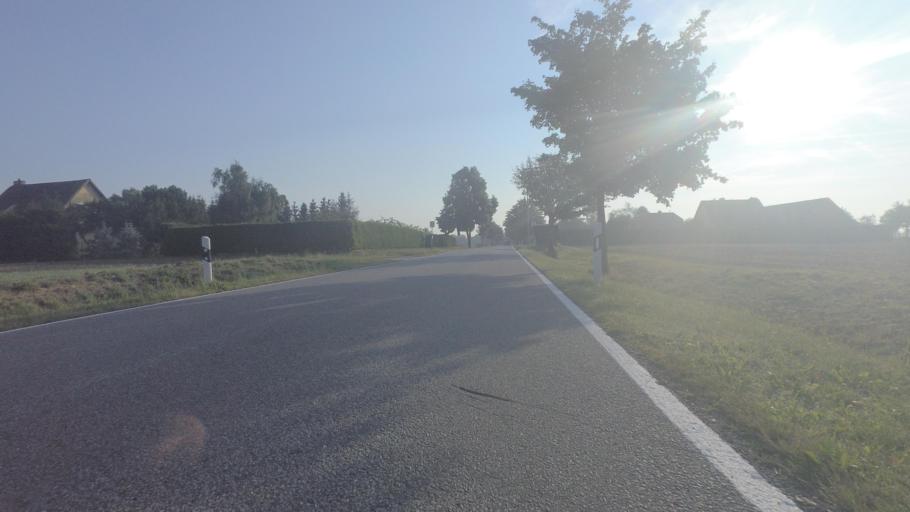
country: DE
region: Mecklenburg-Vorpommern
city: Demmin
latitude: 53.9291
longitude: 13.0844
